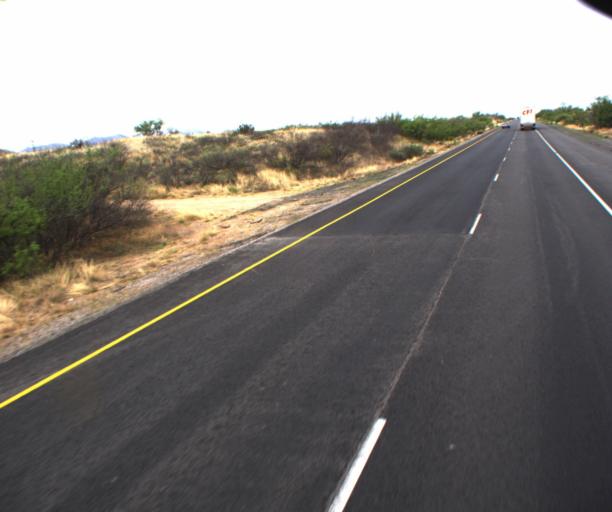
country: US
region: Arizona
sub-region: Cochise County
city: Mescal
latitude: 31.9725
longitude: -110.4848
